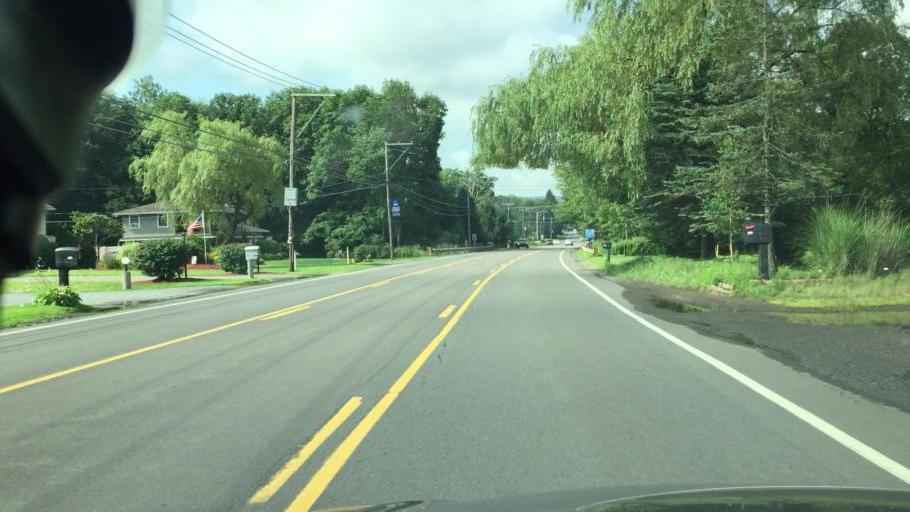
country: US
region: Pennsylvania
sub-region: Luzerne County
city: Mountain Top
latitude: 41.1157
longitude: -75.9122
